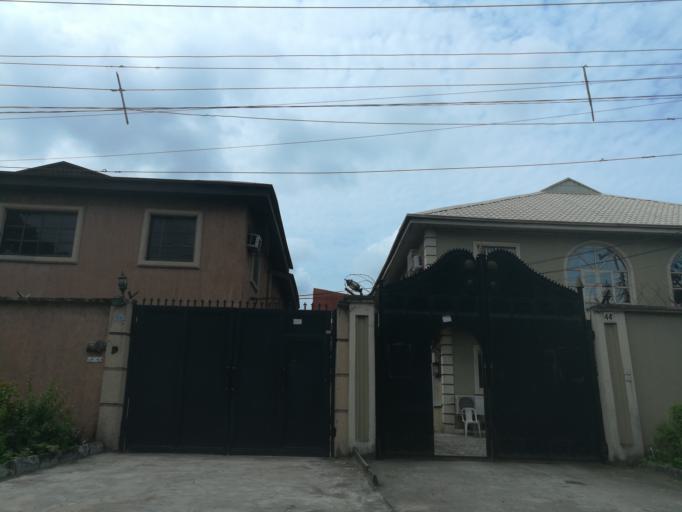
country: NG
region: Lagos
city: Somolu
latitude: 6.5471
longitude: 3.3866
